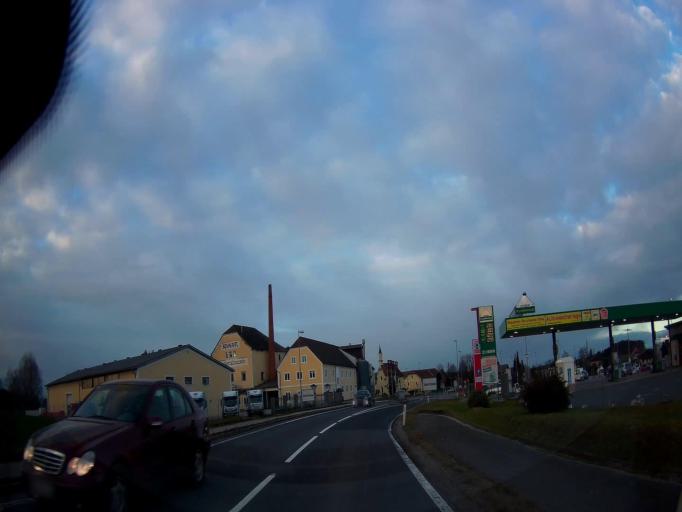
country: AT
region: Salzburg
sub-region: Politischer Bezirk Salzburg-Umgebung
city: Dorfbeuern
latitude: 48.0890
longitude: 12.9915
